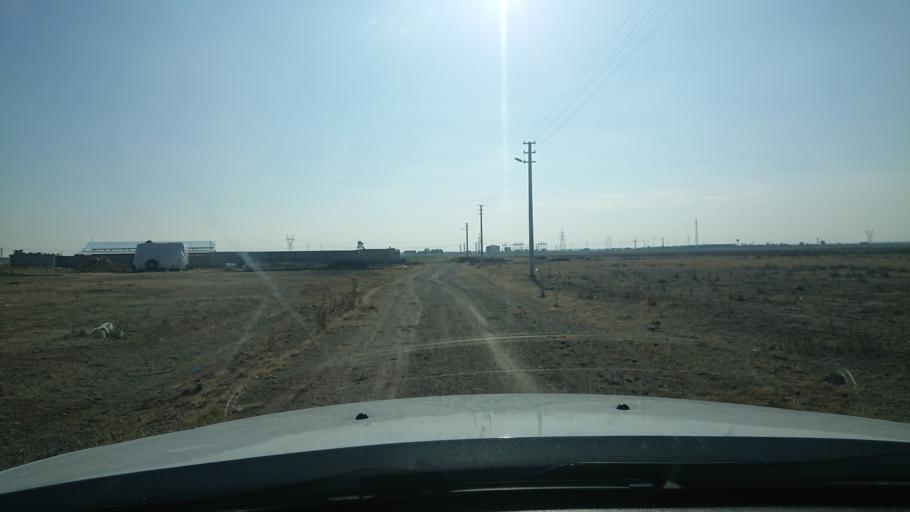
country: TR
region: Aksaray
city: Sultanhani
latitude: 38.2601
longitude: 33.4719
